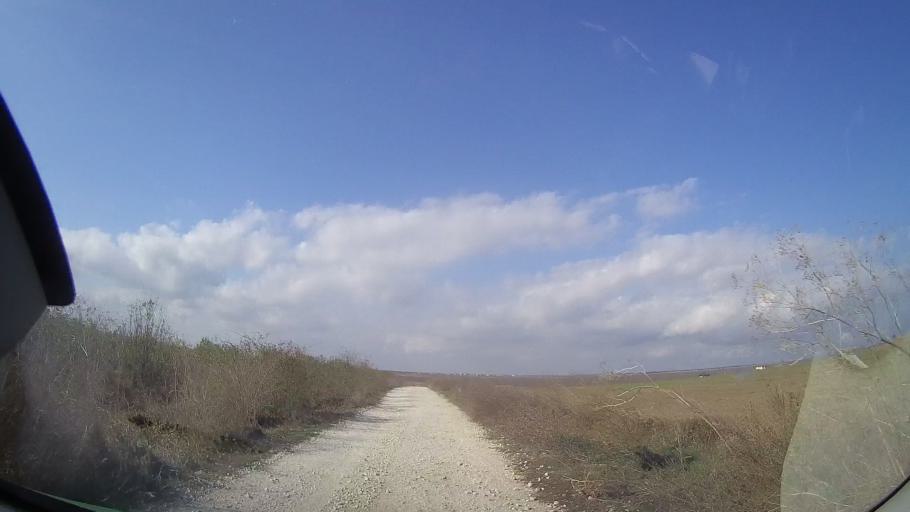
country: RO
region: Constanta
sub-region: Comuna Douazeci si Trei August
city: Douazeci si Trei August
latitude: 43.9050
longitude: 28.6164
